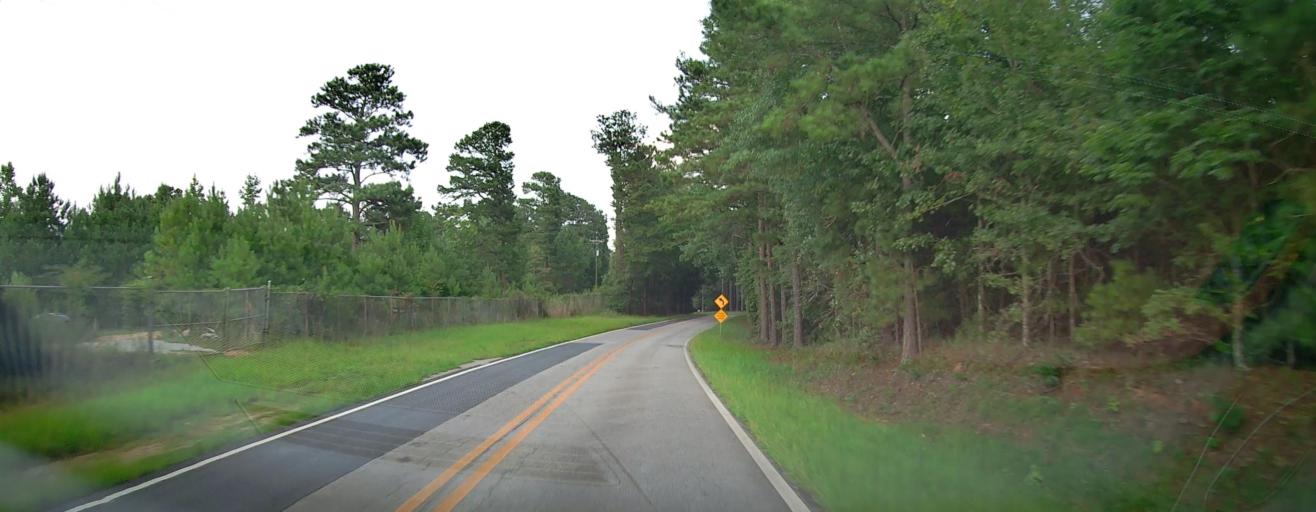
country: US
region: Georgia
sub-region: Monroe County
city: Forsyth
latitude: 32.9763
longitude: -83.7990
